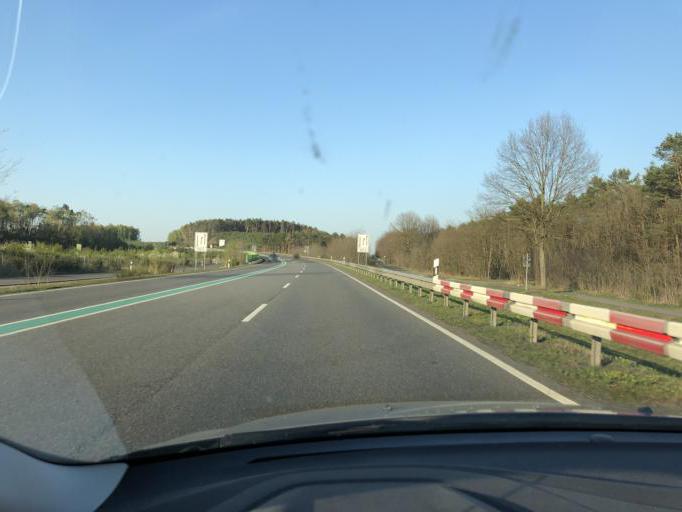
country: DE
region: Brandenburg
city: Schwarzbach
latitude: 51.4883
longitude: 13.9368
